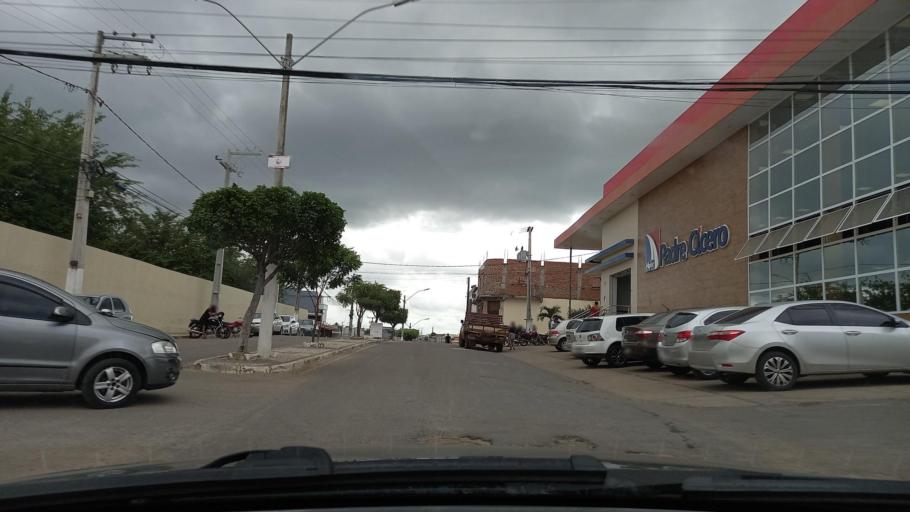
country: BR
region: Sergipe
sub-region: Caninde De Sao Francisco
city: Caninde de Sao Francisco
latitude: -9.6625
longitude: -37.7886
